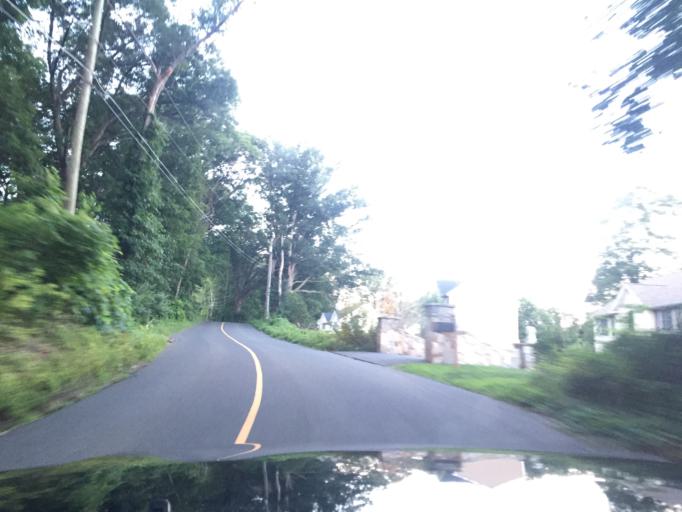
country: US
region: Connecticut
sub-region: Fairfield County
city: Bethel
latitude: 41.4092
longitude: -73.3760
